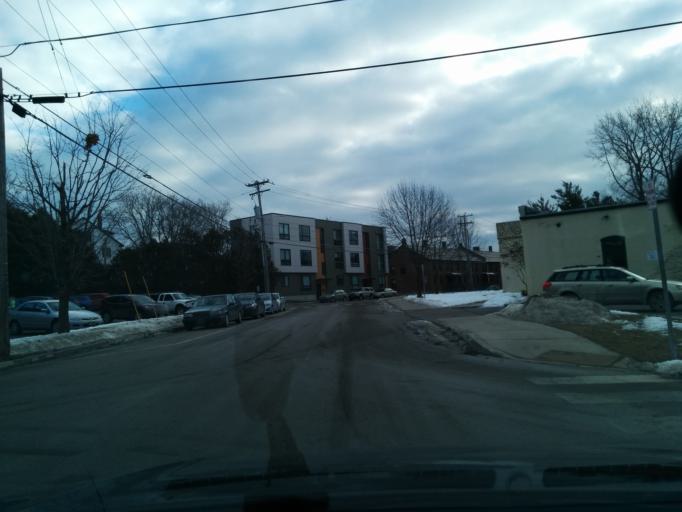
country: US
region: Vermont
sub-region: Chittenden County
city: Winooski
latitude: 44.4909
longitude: -73.1905
